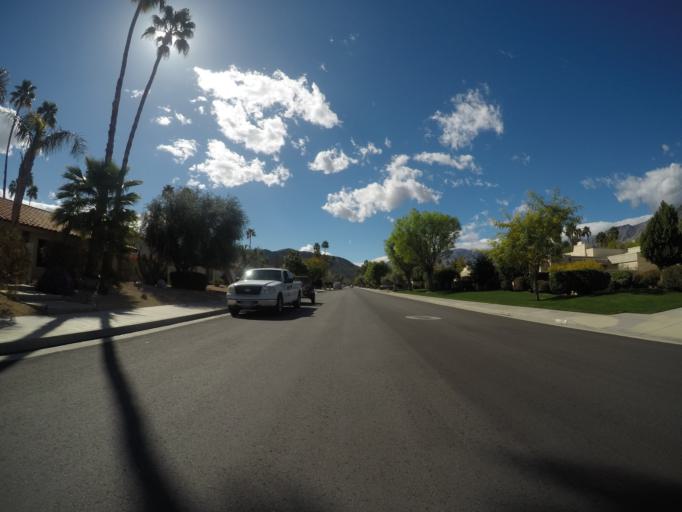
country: US
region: California
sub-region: Riverside County
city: Palm Springs
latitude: 33.8042
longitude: -116.5238
